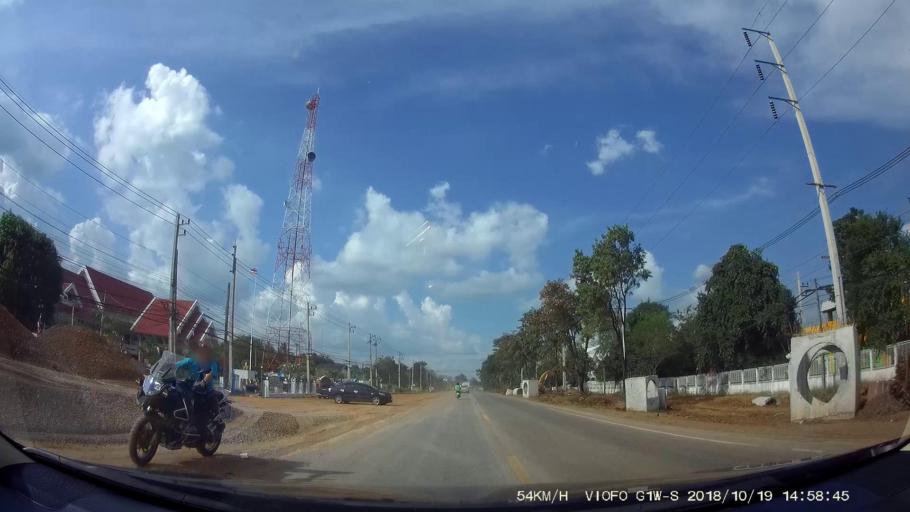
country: TH
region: Chaiyaphum
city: Phu Khiao
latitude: 16.3775
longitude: 102.1293
